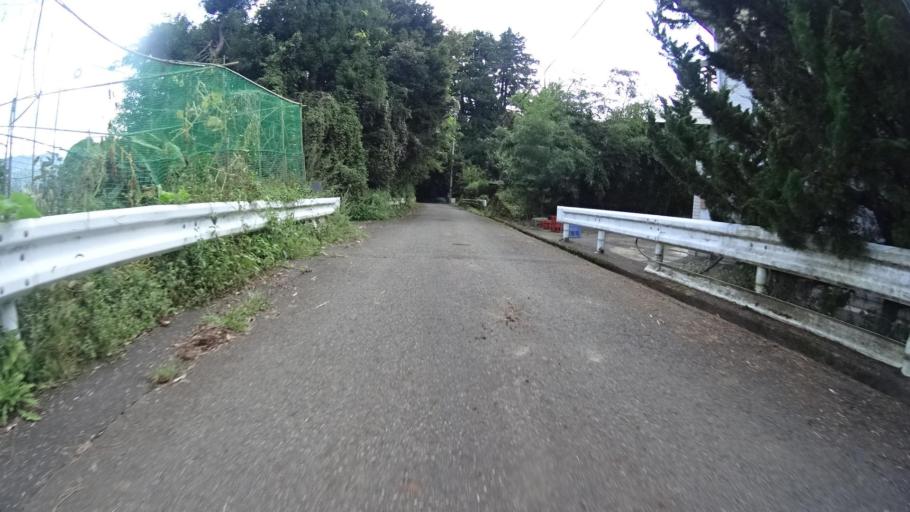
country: JP
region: Yamanashi
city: Uenohara
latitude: 35.7426
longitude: 139.0638
